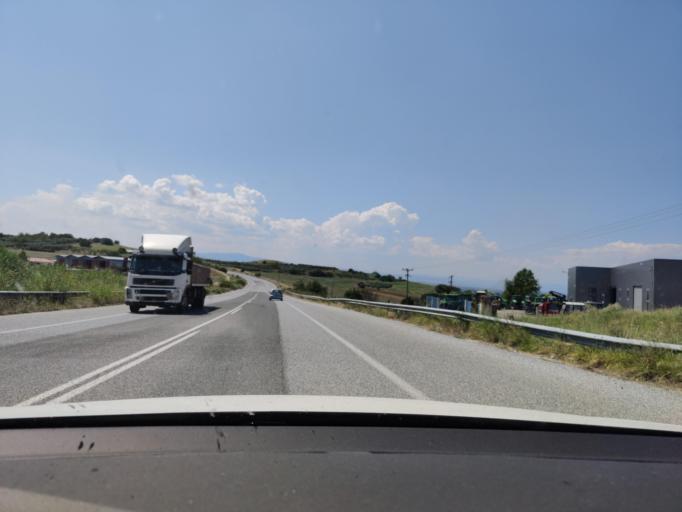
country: GR
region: Central Macedonia
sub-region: Nomos Serron
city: Draviskos
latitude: 40.9310
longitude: 23.8609
